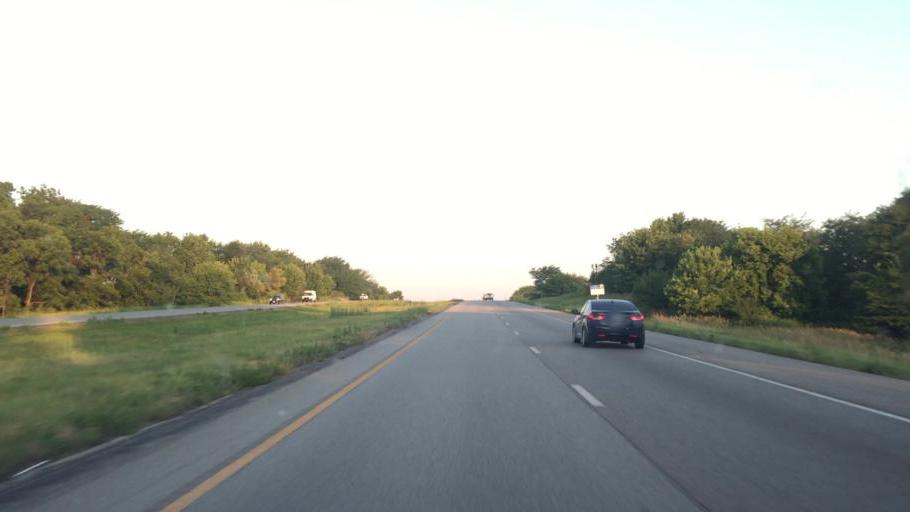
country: US
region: Missouri
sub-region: Clay County
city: Smithville
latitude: 39.3110
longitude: -94.5249
